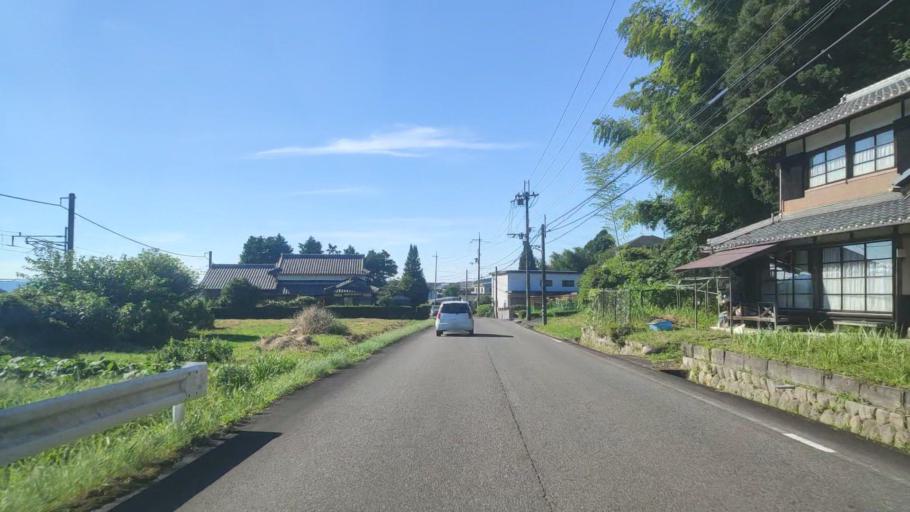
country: JP
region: Shiga Prefecture
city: Minakuchicho-matoba
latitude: 34.8846
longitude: 136.2336
